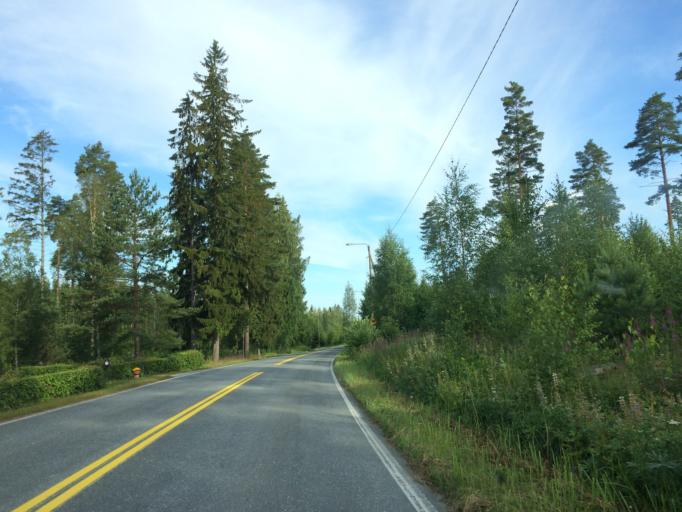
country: FI
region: Haeme
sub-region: Haemeenlinna
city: Janakkala
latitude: 60.9306
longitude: 24.5660
